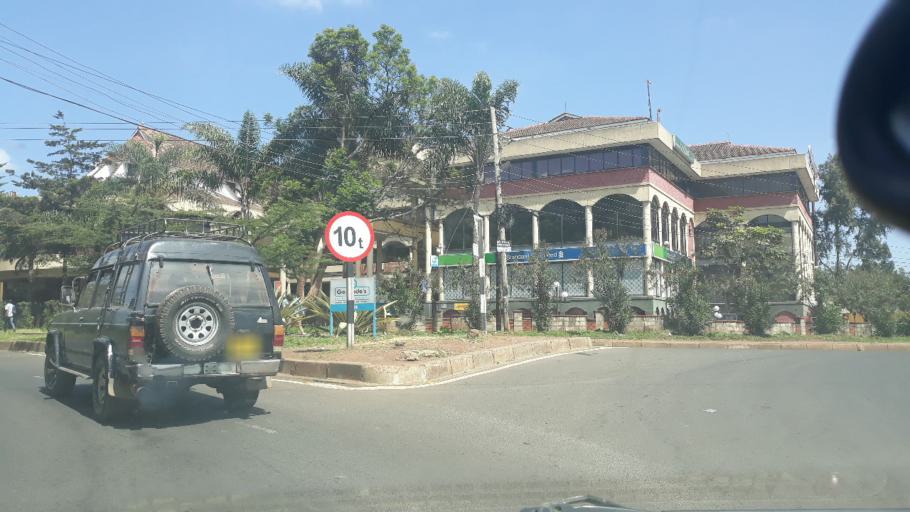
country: KE
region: Nairobi Area
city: Pumwani
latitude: -1.2620
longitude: 36.8399
